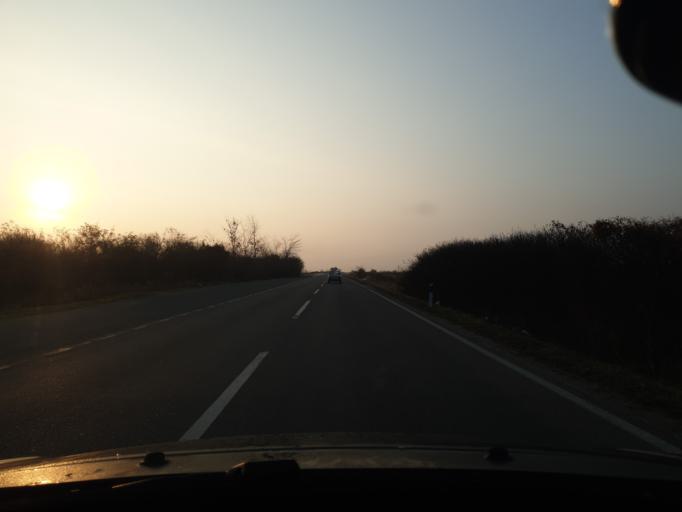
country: RS
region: Central Serbia
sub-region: Jablanicki Okrug
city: Leskovac
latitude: 42.9561
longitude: 21.9869
